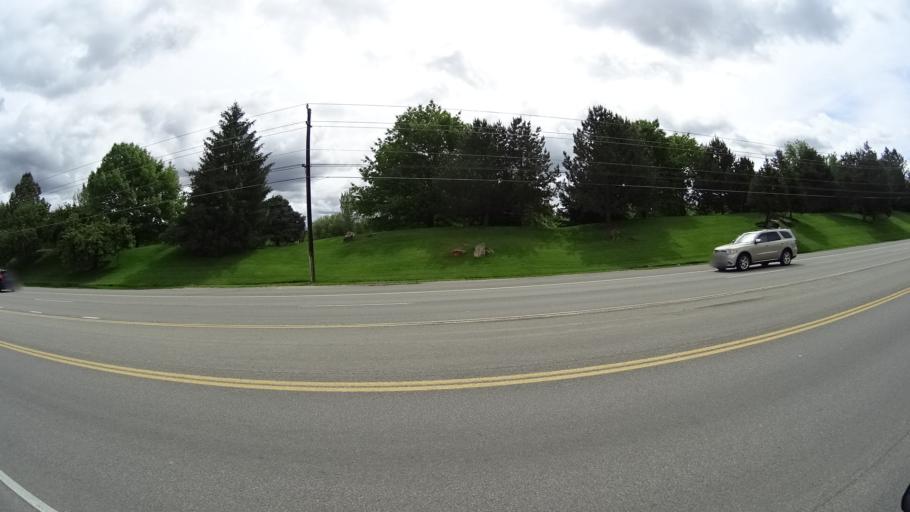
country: US
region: Idaho
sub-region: Ada County
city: Eagle
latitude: 43.6806
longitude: -116.3543
